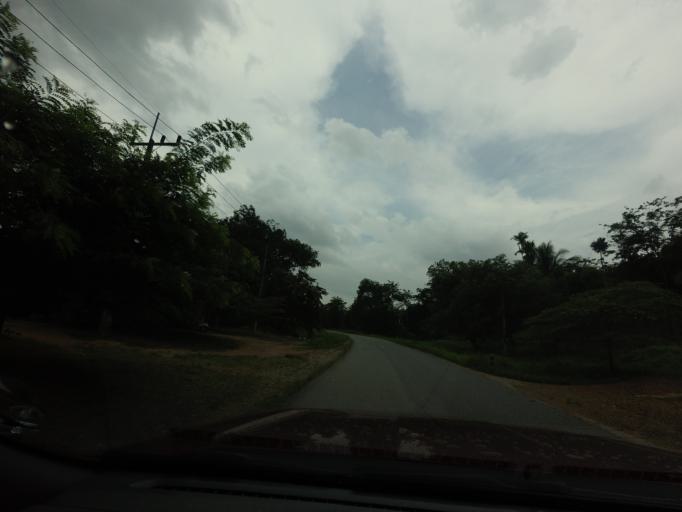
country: TH
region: Yala
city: Ban Nang Sata
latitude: 6.2058
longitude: 101.2354
